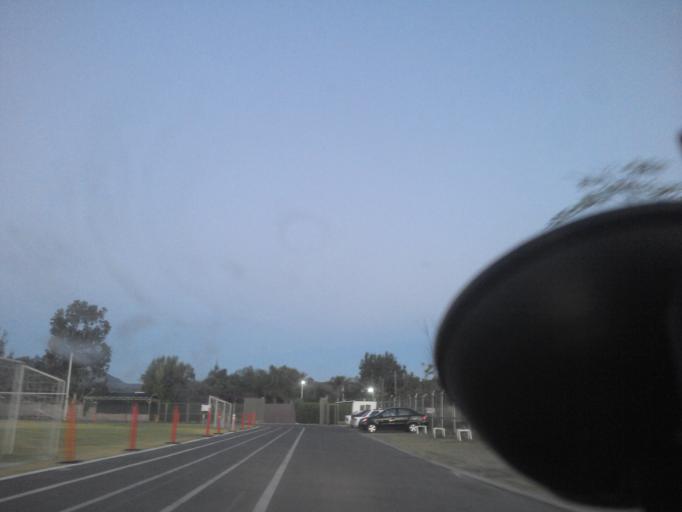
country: MX
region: Jalisco
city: Nuevo Mexico
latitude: 20.6997
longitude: -103.4698
